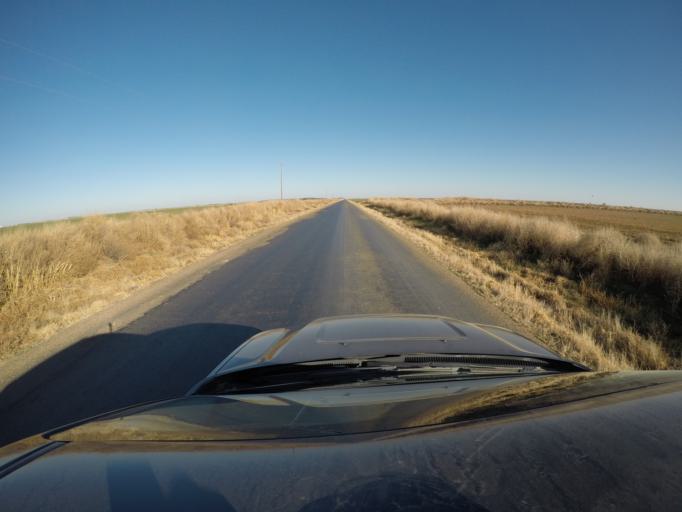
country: US
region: New Mexico
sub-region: Curry County
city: Texico
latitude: 34.3027
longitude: -103.0878
